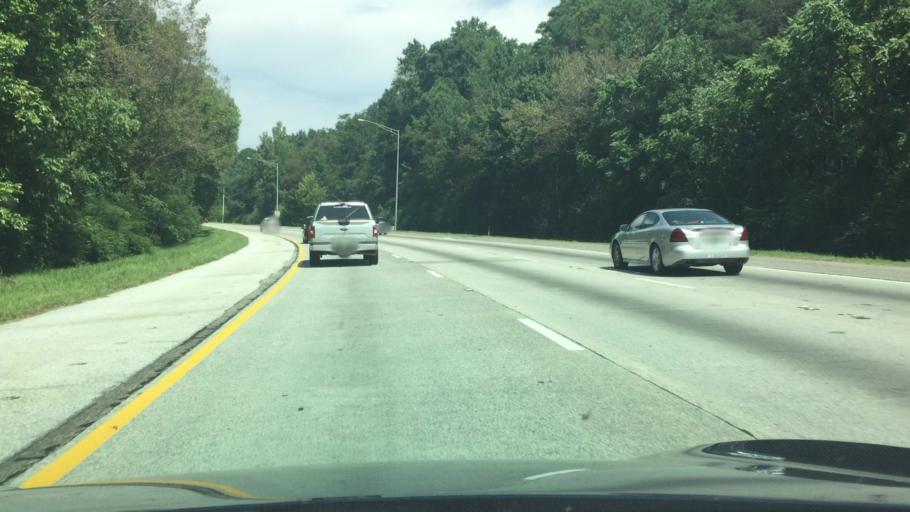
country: US
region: Alabama
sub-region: Jefferson County
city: Hoover
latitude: 33.4235
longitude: -86.8146
